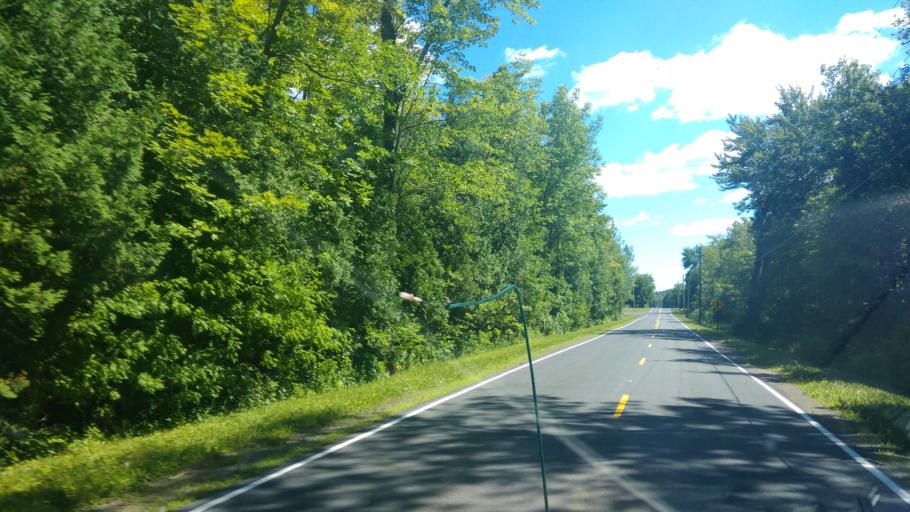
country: US
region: New York
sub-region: Wayne County
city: Sodus
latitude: 43.1842
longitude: -77.0501
